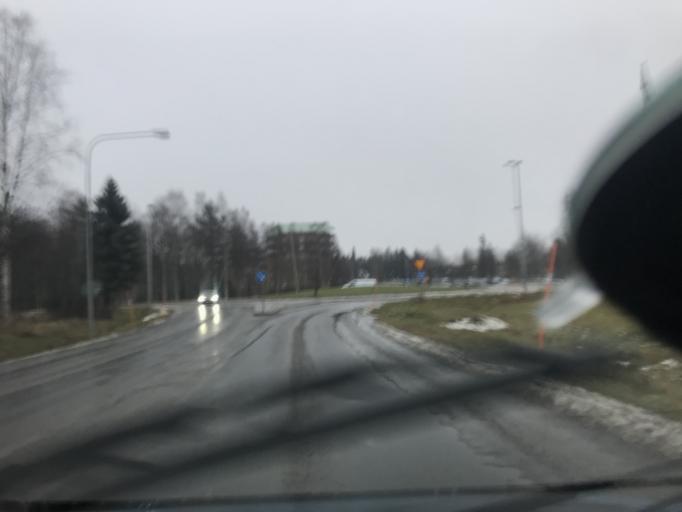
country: SE
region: Norrbotten
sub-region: Lulea Kommun
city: Lulea
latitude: 65.6185
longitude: 22.1286
